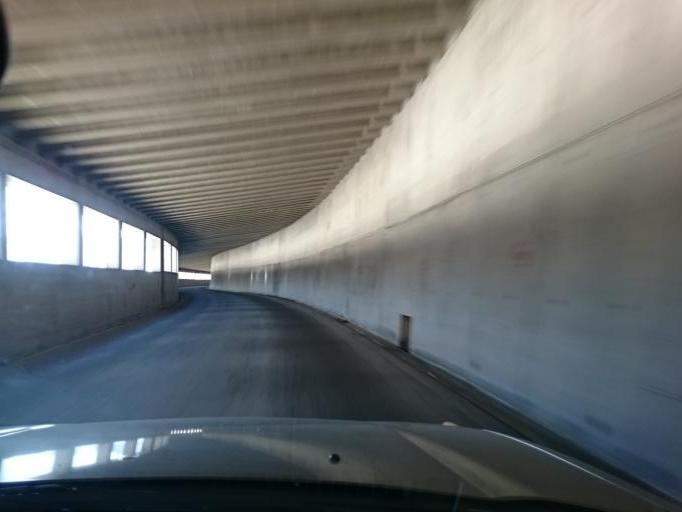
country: IT
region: Lombardy
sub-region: Provincia di Sondrio
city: Livigno
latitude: 46.5629
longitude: 10.1480
